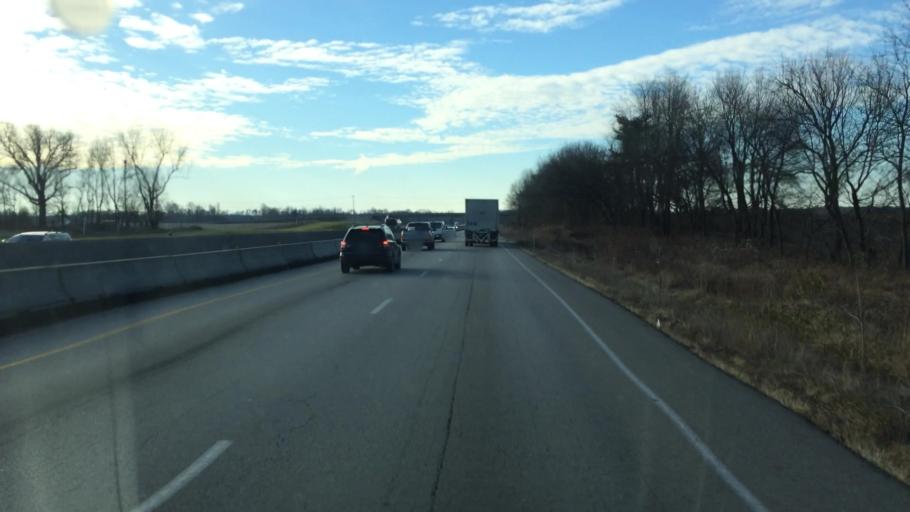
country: US
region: Kentucky
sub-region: Hardin County
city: Elizabethtown
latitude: 37.5775
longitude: -85.8729
